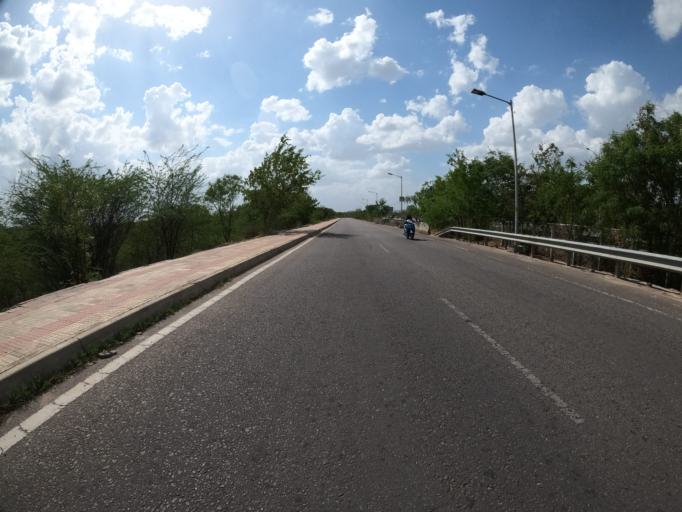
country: IN
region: Telangana
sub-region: Hyderabad
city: Hyderabad
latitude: 17.3573
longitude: 78.3555
